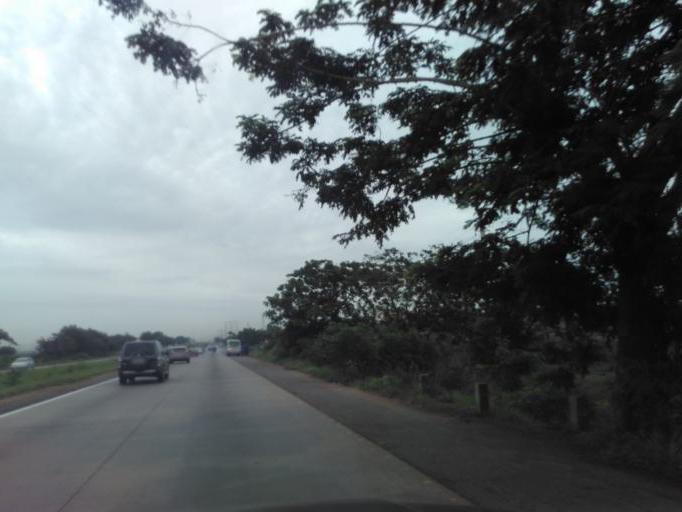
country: GH
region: Greater Accra
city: Tema
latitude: 5.6760
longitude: -0.0410
